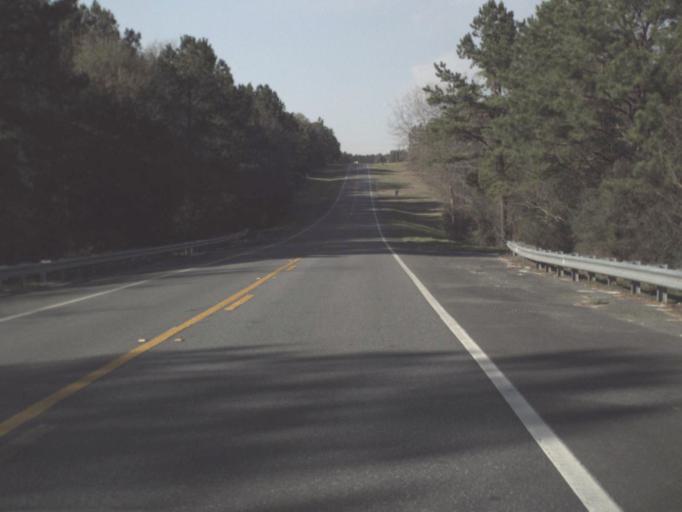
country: US
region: Florida
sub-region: Calhoun County
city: Blountstown
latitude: 30.5005
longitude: -85.2002
